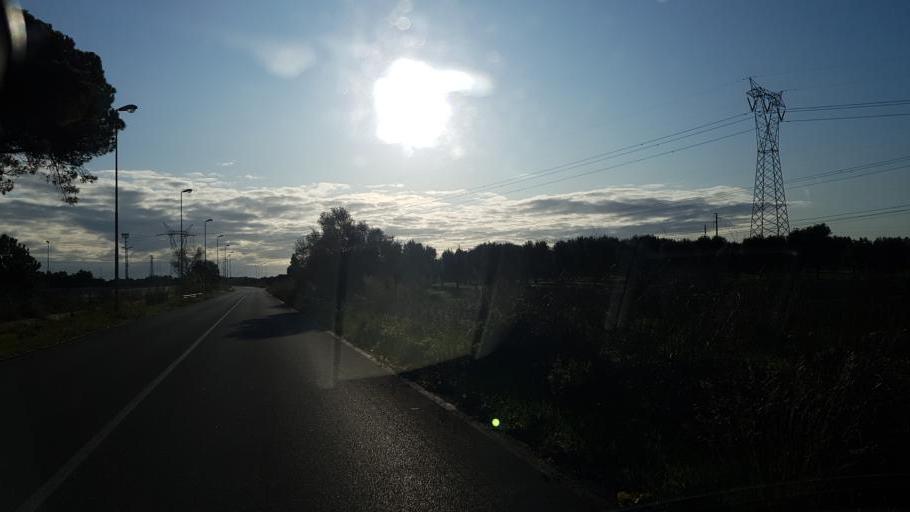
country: IT
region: Apulia
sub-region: Provincia di Brindisi
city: San Pietro Vernotico
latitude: 40.5575
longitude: 18.0255
